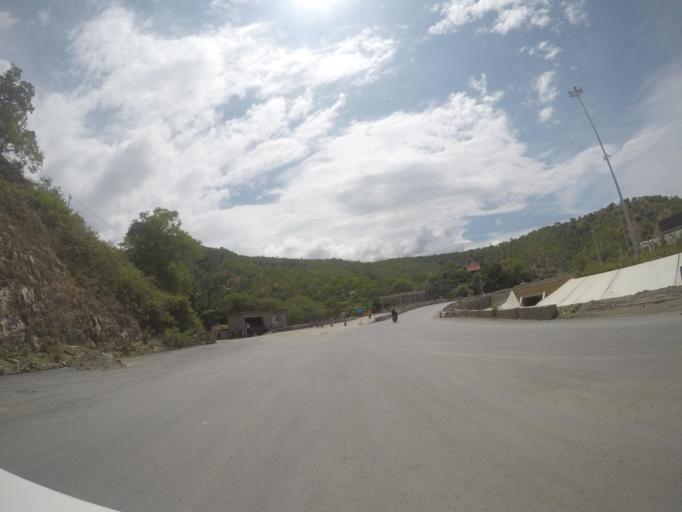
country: TL
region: Dili
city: Dili
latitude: -8.5751
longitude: 125.4760
